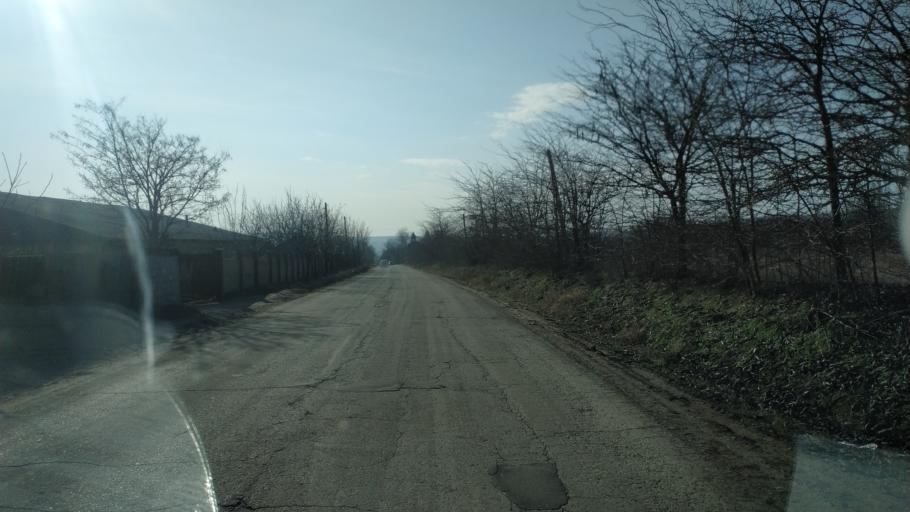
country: MD
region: Chisinau
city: Singera
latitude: 46.8433
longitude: 29.0255
